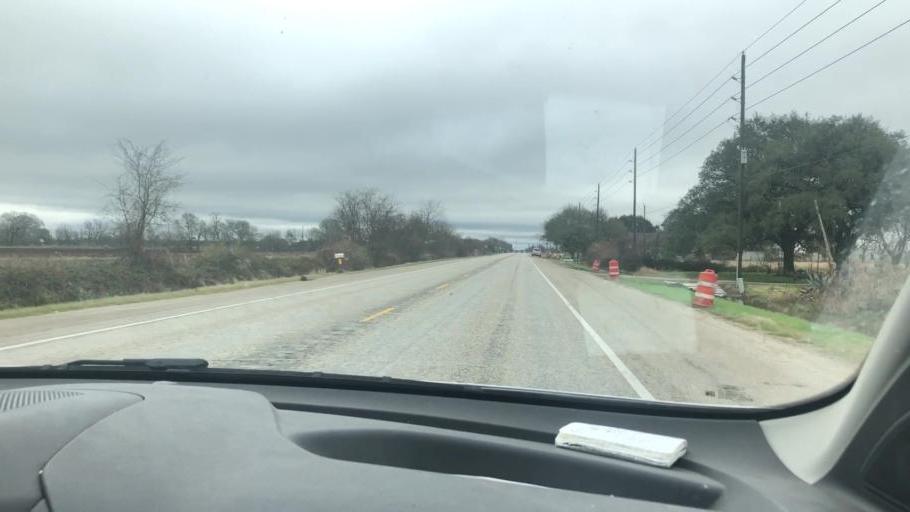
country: US
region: Texas
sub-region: Wharton County
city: Wharton
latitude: 29.2663
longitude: -96.0575
